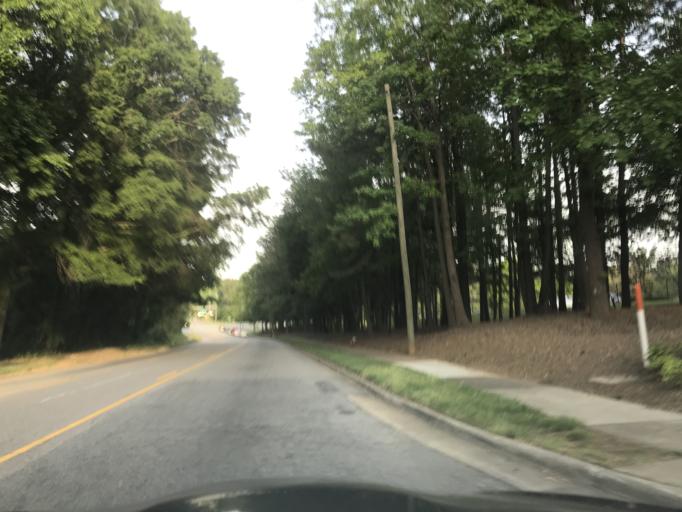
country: US
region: North Carolina
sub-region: Wake County
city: Raleigh
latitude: 35.7430
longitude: -78.6430
